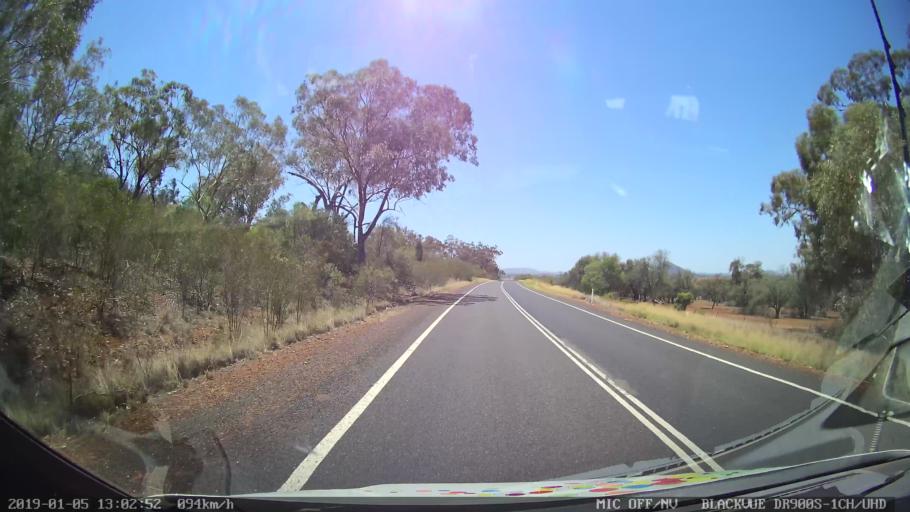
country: AU
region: New South Wales
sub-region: Gunnedah
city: Gunnedah
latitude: -31.1128
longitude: 149.8183
